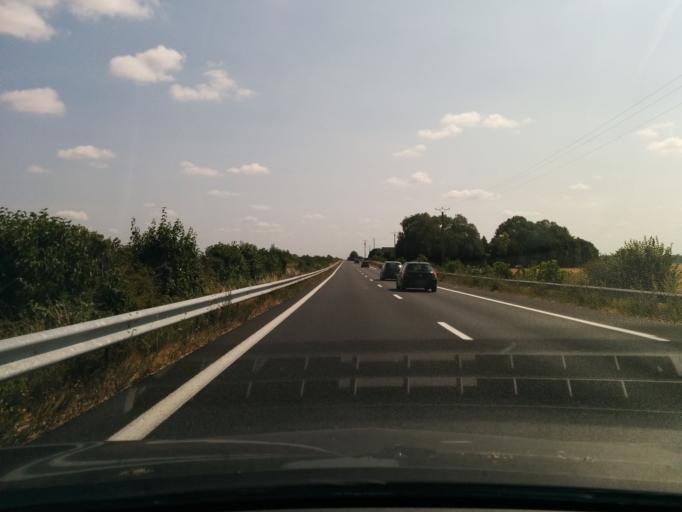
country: FR
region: Centre
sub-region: Departement de l'Indre
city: Montierchaume
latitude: 46.9487
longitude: 1.7542
